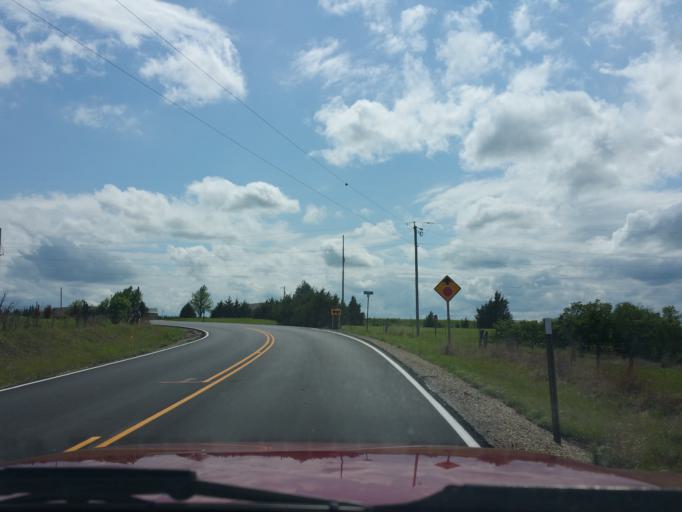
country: US
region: Kansas
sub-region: Riley County
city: Manhattan
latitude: 39.2652
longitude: -96.6810
